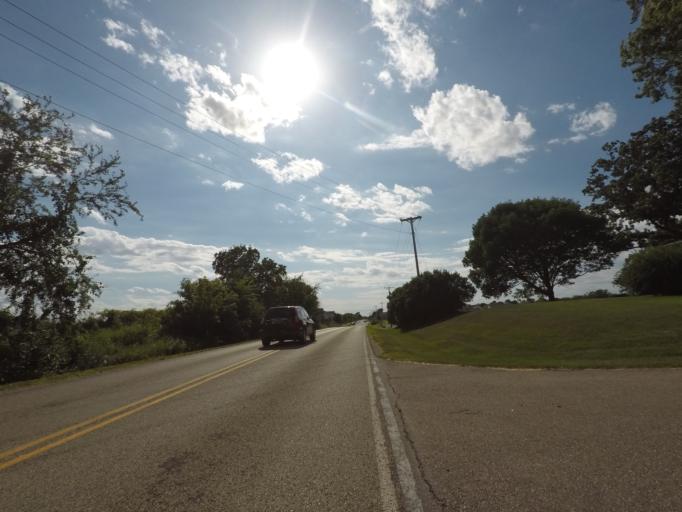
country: US
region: Wisconsin
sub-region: Dane County
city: Middleton
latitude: 43.0675
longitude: -89.5445
